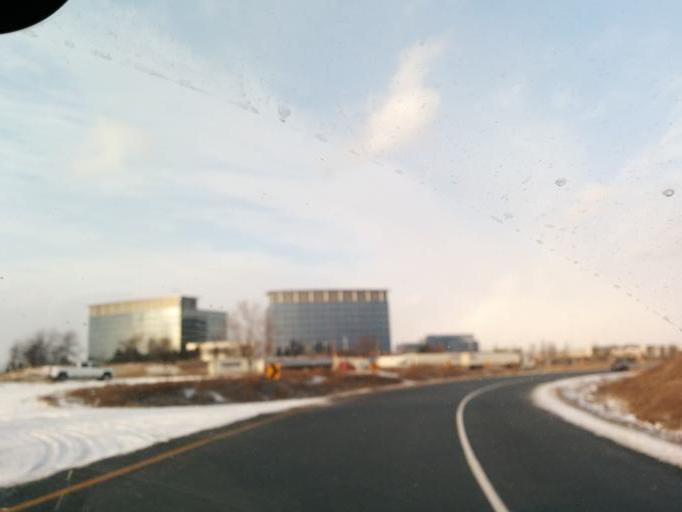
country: CA
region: Ontario
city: Brampton
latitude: 43.6051
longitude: -79.7443
